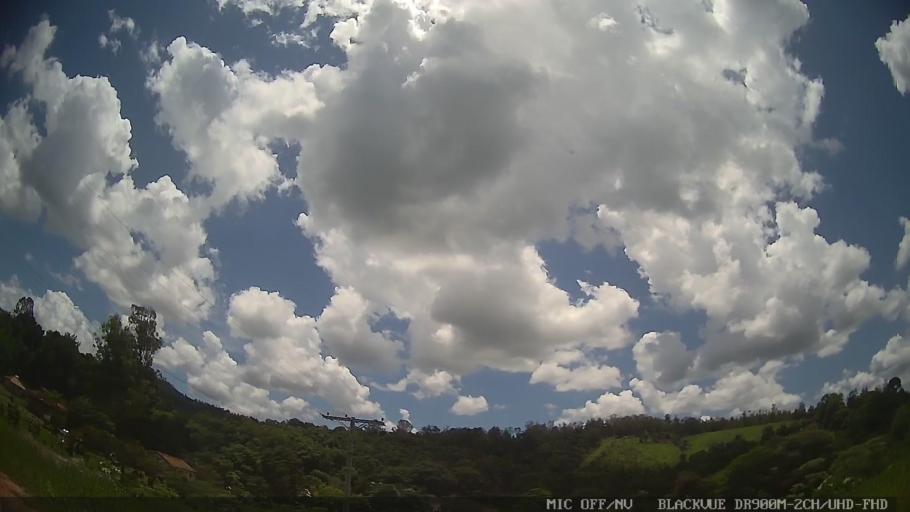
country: BR
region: Sao Paulo
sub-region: Amparo
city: Amparo
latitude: -22.6823
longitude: -46.7415
